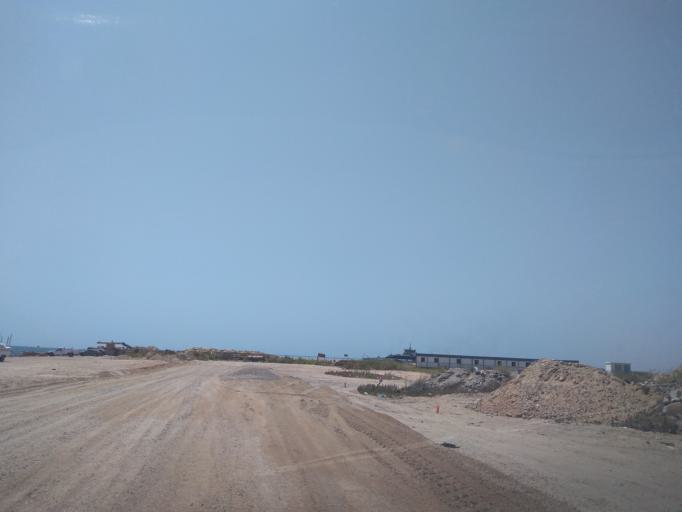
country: TN
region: Safaqis
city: Al Qarmadah
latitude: 34.7244
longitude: 10.7807
